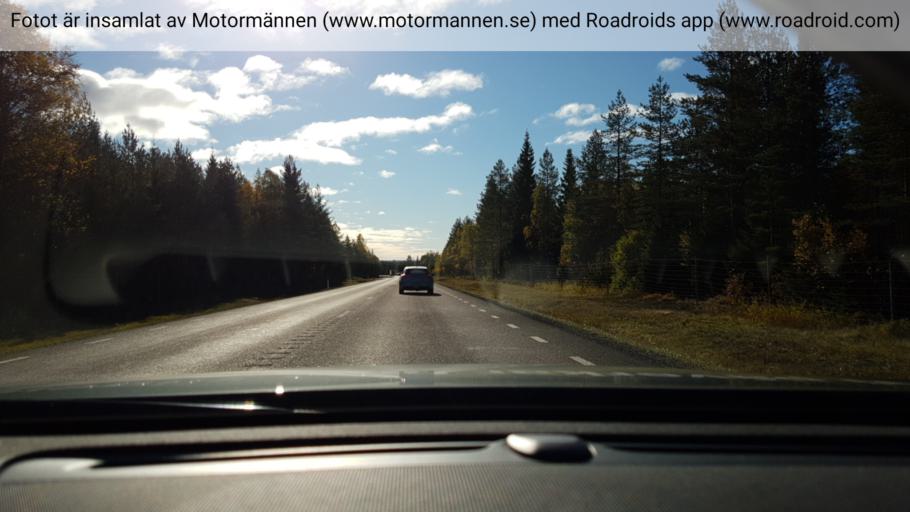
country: SE
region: Vaesterbotten
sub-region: Skelleftea Kommun
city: Burea
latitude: 64.4237
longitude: 21.2849
